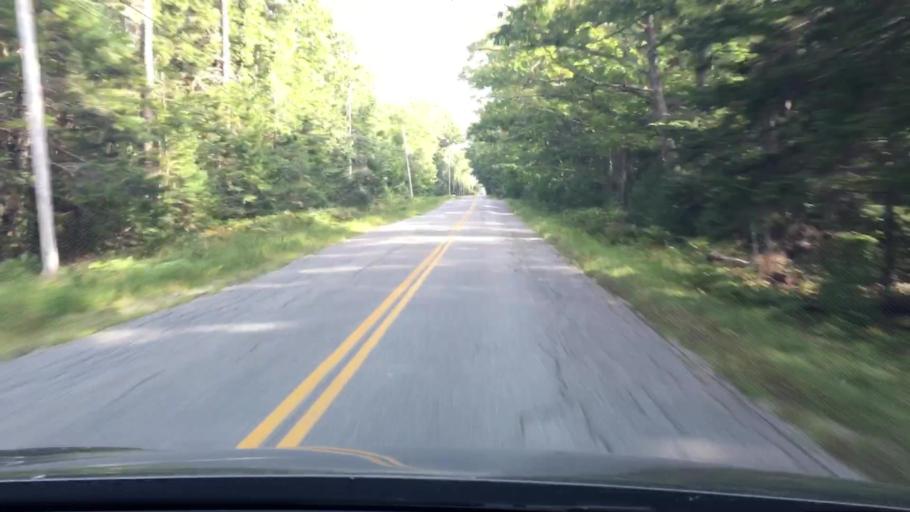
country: US
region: Maine
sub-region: Hancock County
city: Bucksport
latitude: 44.5347
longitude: -68.7935
